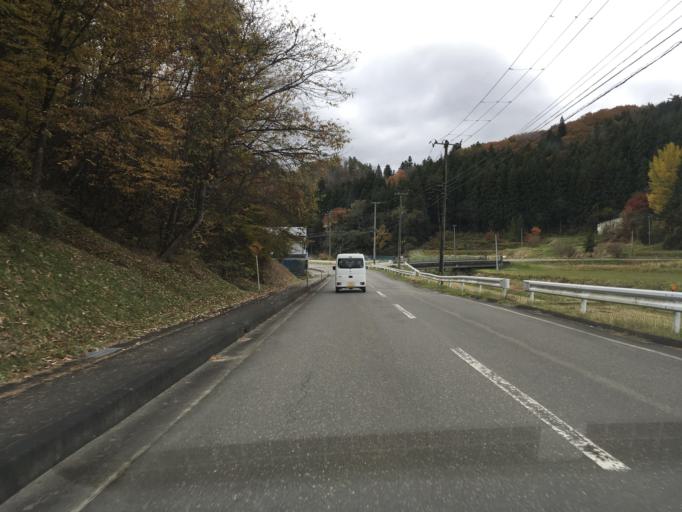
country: JP
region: Iwate
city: Mizusawa
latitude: 39.0591
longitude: 141.3619
